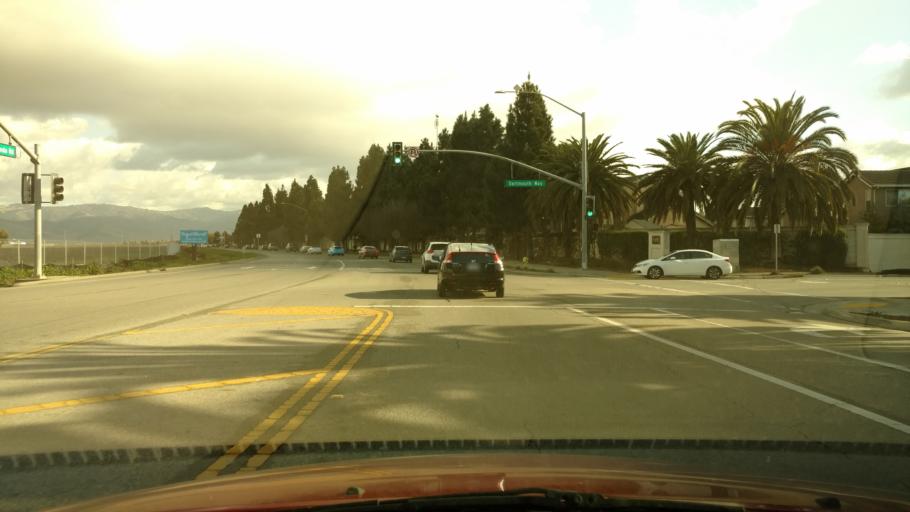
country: US
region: California
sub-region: Monterey County
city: Boronda
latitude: 36.7180
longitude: -121.6491
